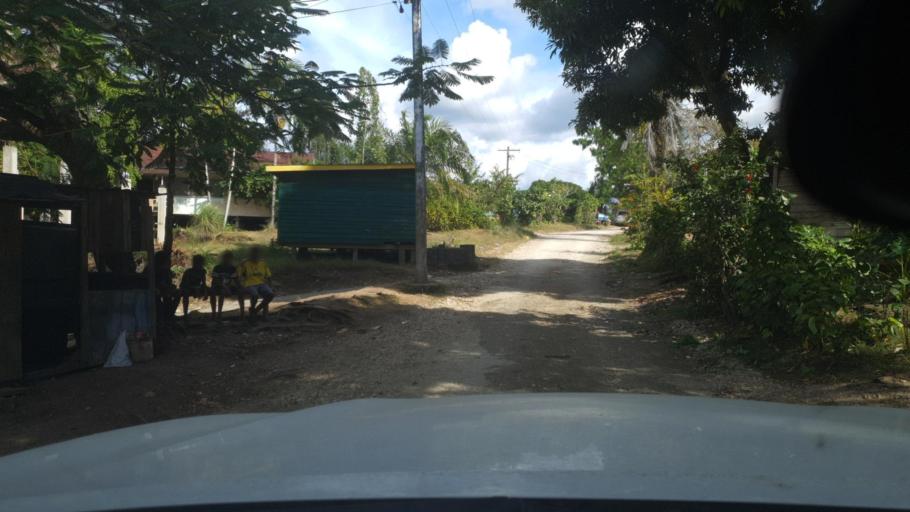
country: SB
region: Guadalcanal
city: Honiara
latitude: -9.4356
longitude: 159.9477
